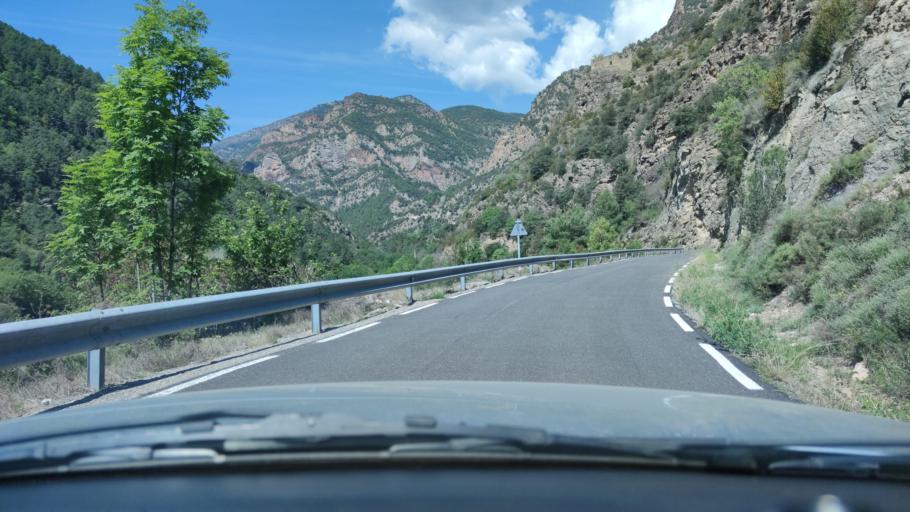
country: ES
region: Catalonia
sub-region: Provincia de Lleida
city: Coll de Nargo
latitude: 42.2963
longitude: 1.3115
